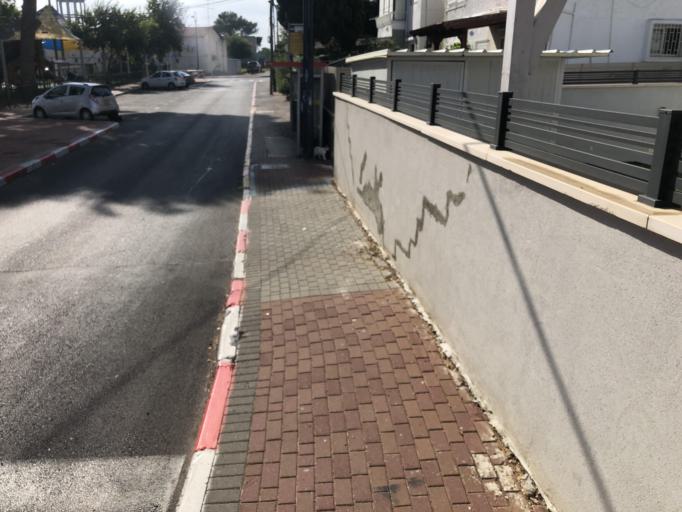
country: IL
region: Northern District
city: `Akko
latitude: 32.9383
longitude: 35.0935
